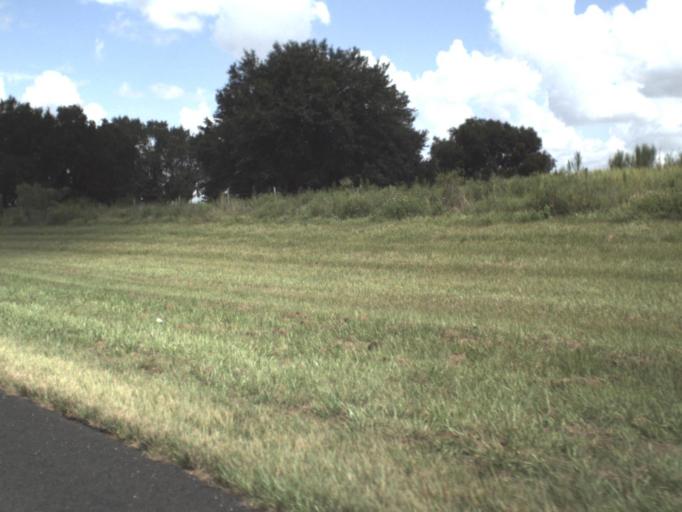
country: US
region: Florida
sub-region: Polk County
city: Fort Meade
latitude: 27.8081
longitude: -81.8196
